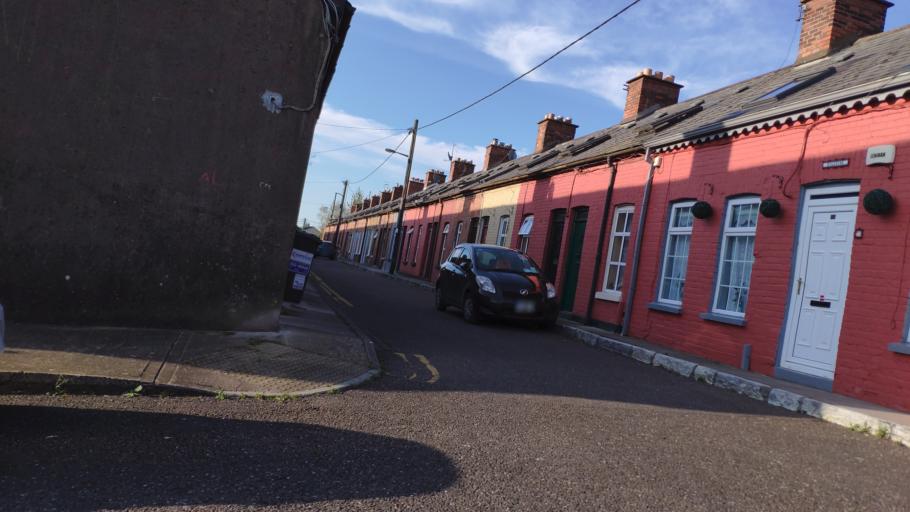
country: IE
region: Munster
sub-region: County Cork
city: Cork
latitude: 51.9063
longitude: -8.4698
